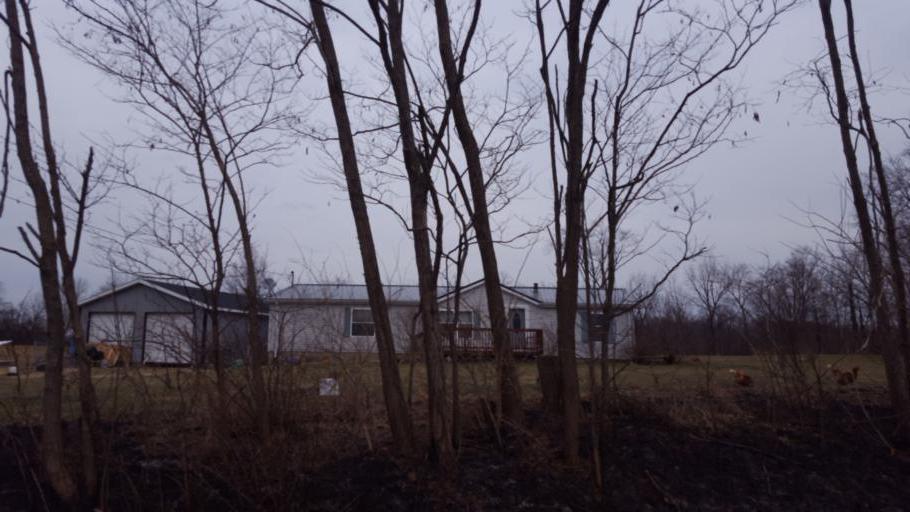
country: US
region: Ohio
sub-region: Morrow County
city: Mount Gilead
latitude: 40.6352
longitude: -82.7951
